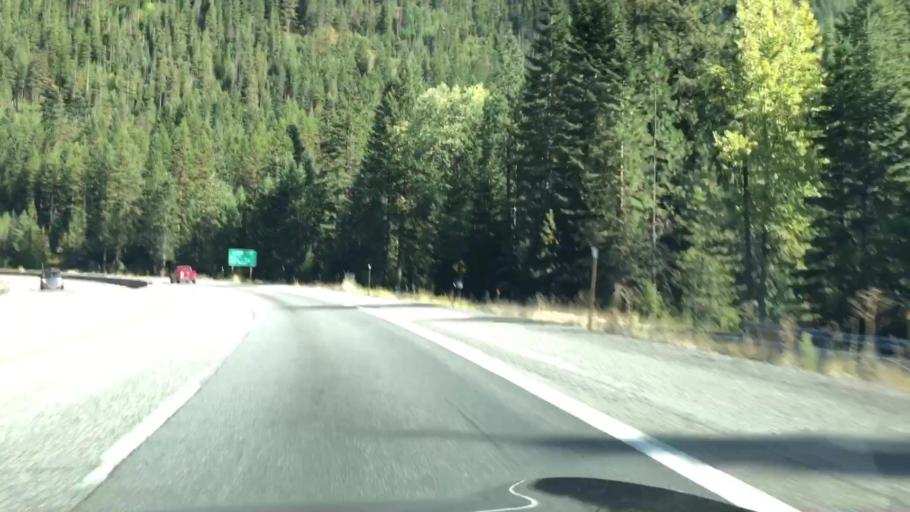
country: US
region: Idaho
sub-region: Shoshone County
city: Wallace
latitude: 47.4610
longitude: -115.8254
